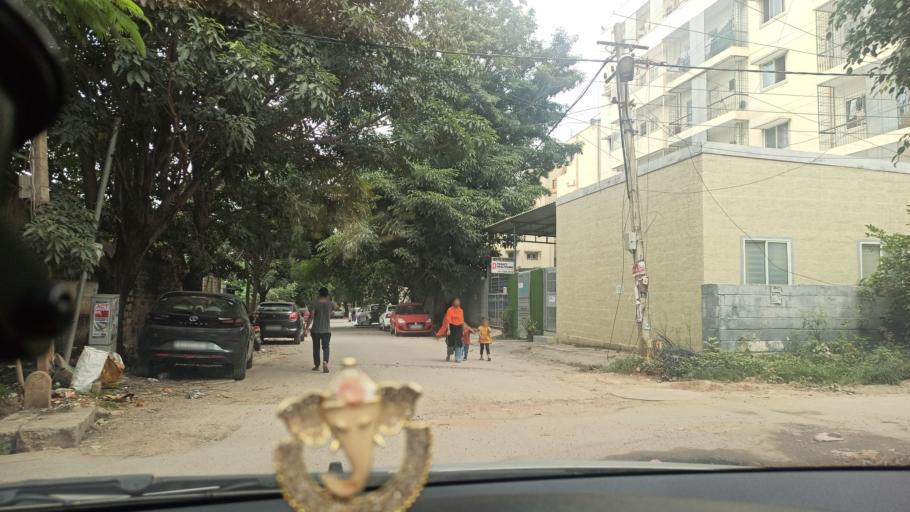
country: IN
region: Karnataka
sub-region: Bangalore Urban
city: Bangalore
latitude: 12.9197
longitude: 77.6472
